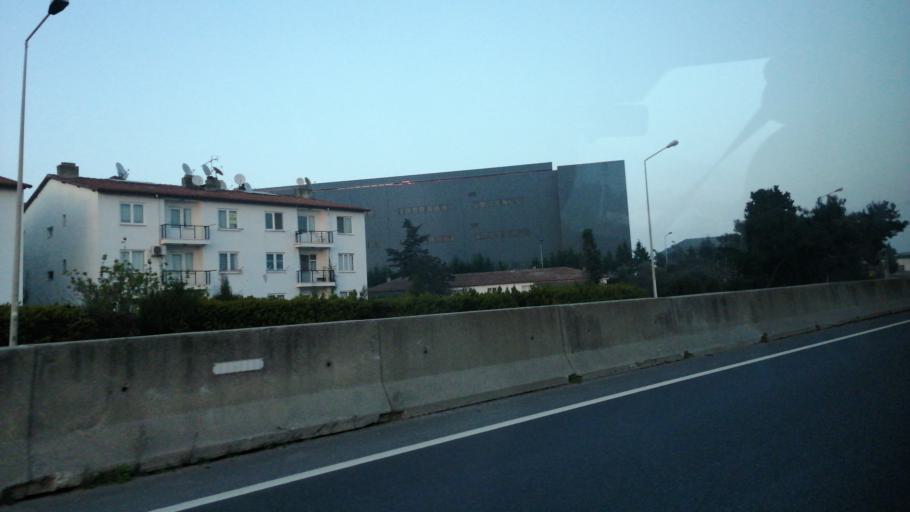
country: TR
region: Yalova
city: Taskopru
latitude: 40.6876
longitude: 29.4299
